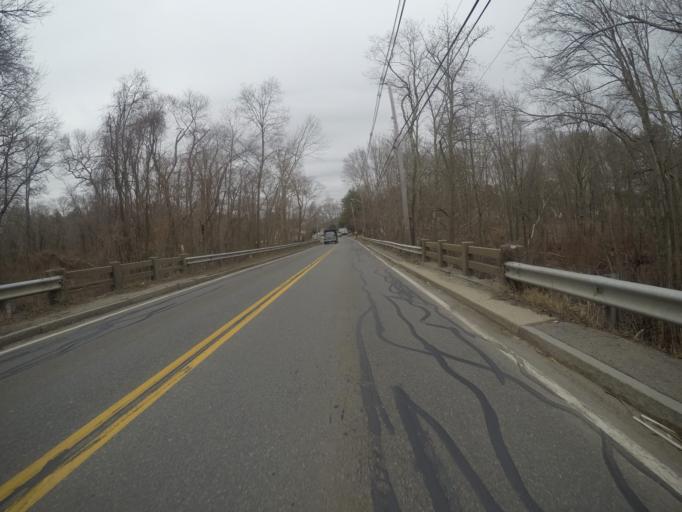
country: US
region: Massachusetts
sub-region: Bristol County
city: Easton
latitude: 42.0412
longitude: -71.0680
